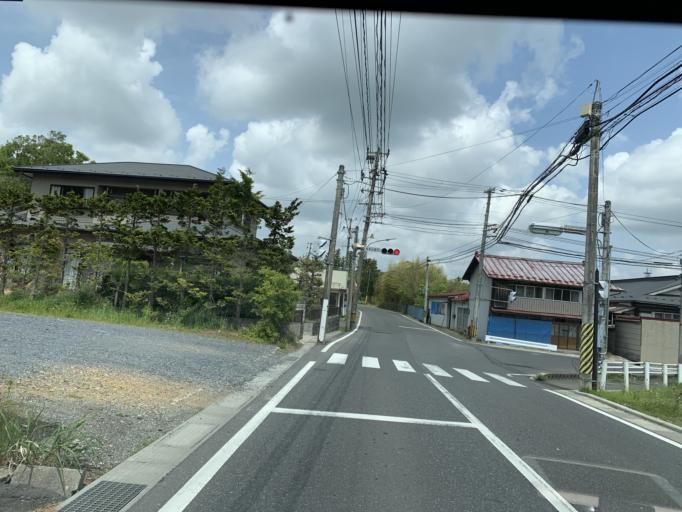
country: JP
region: Miyagi
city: Kogota
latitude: 38.6643
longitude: 141.0655
